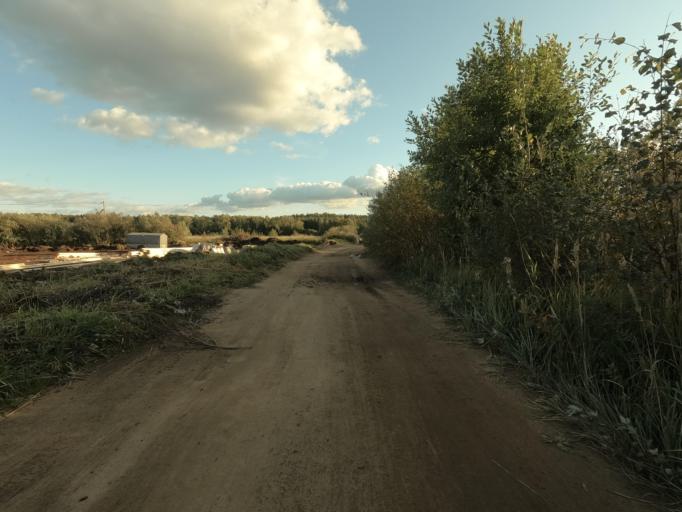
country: RU
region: Leningrad
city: Otradnoye
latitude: 59.8572
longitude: 30.7969
